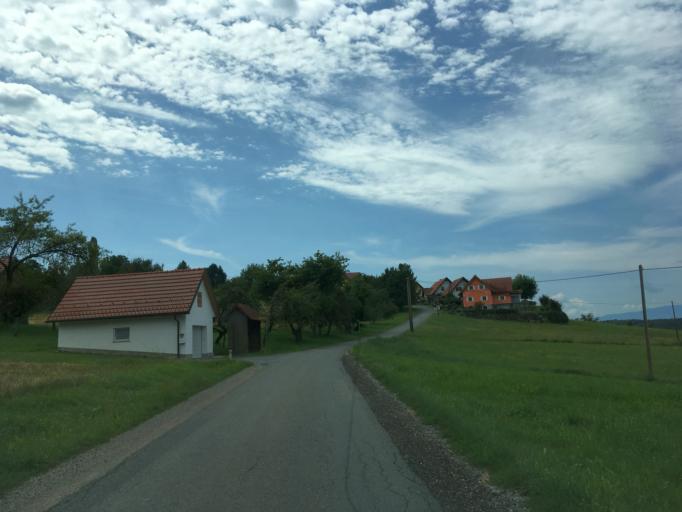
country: AT
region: Styria
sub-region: Politischer Bezirk Leibnitz
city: Kitzeck im Sausal
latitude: 46.7889
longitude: 15.4048
